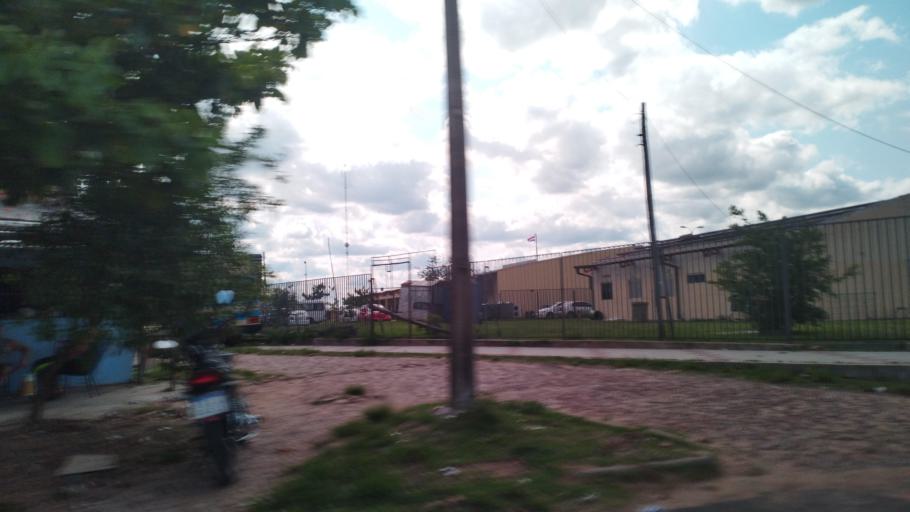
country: PY
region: Asuncion
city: Asuncion
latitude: -25.2779
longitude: -57.6213
